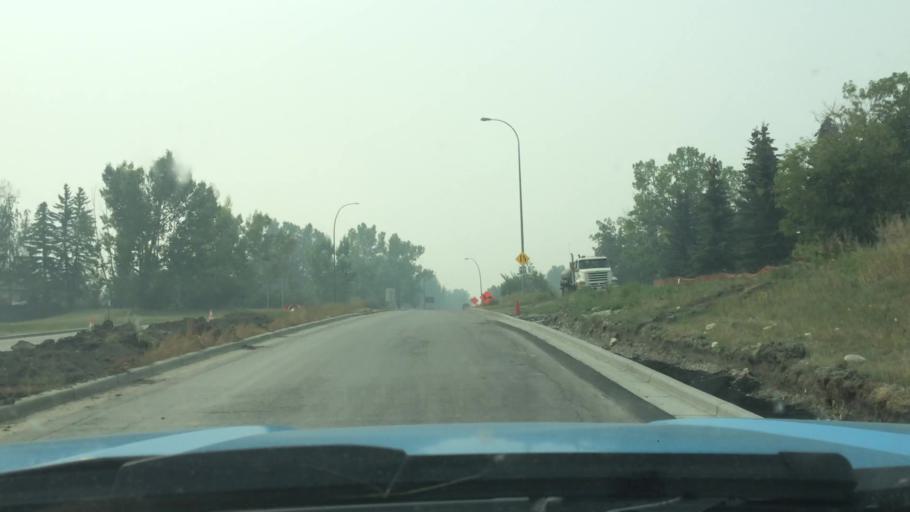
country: CA
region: Alberta
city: Calgary
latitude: 50.9494
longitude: -114.0949
